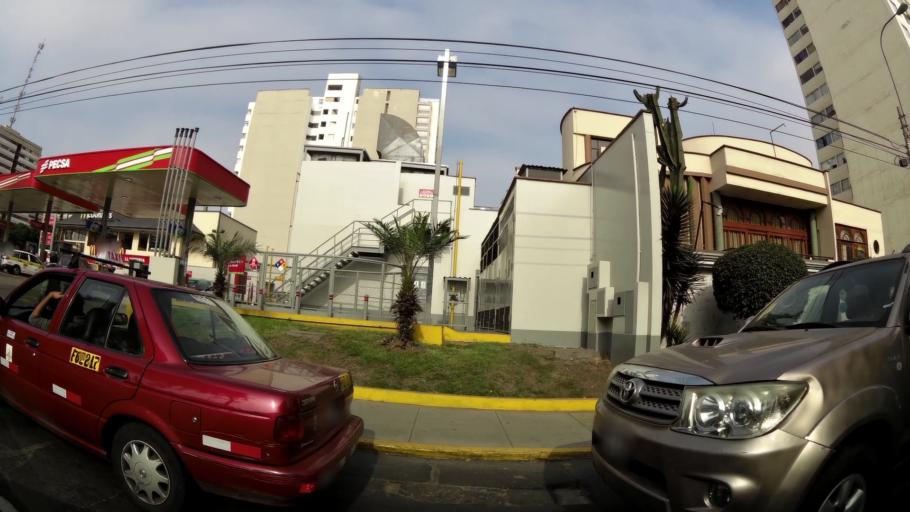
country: PE
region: Lima
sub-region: Lima
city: San Isidro
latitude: -12.0907
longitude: -77.0580
